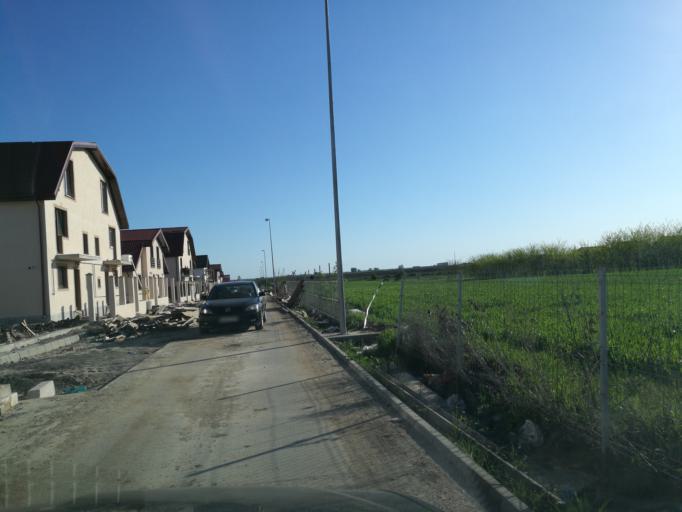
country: RO
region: Ilfov
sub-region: Comuna Vidra
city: Vidra
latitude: 44.2779
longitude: 26.1838
